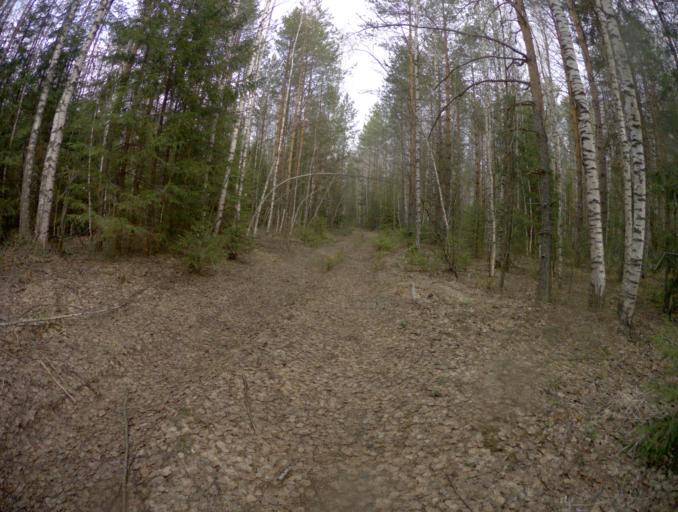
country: RU
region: Vladimir
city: Raduzhnyy
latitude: 55.9525
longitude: 40.2696
